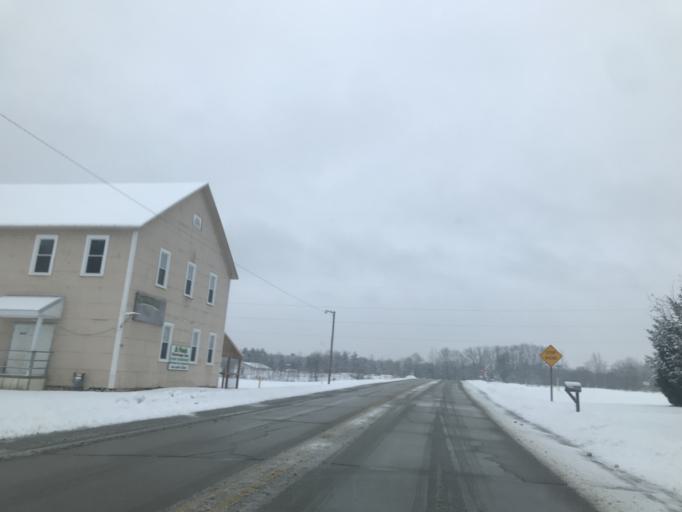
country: US
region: Wisconsin
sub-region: Oconto County
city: Oconto Falls
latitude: 44.8617
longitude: -88.0507
